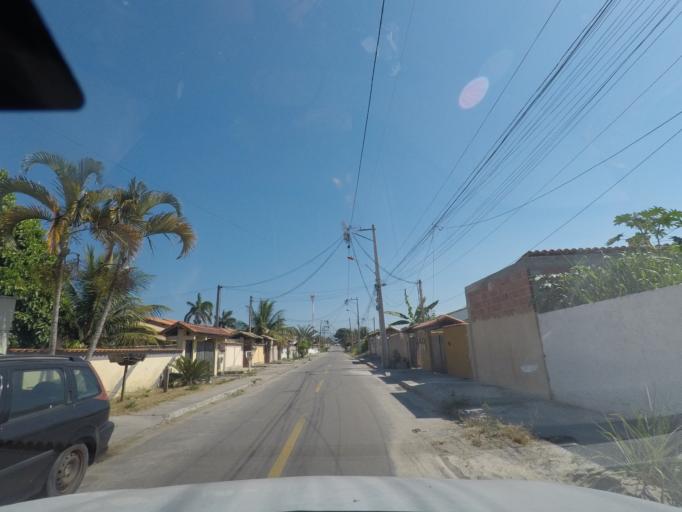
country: BR
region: Rio de Janeiro
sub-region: Niteroi
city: Niteroi
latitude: -22.9606
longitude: -42.9721
